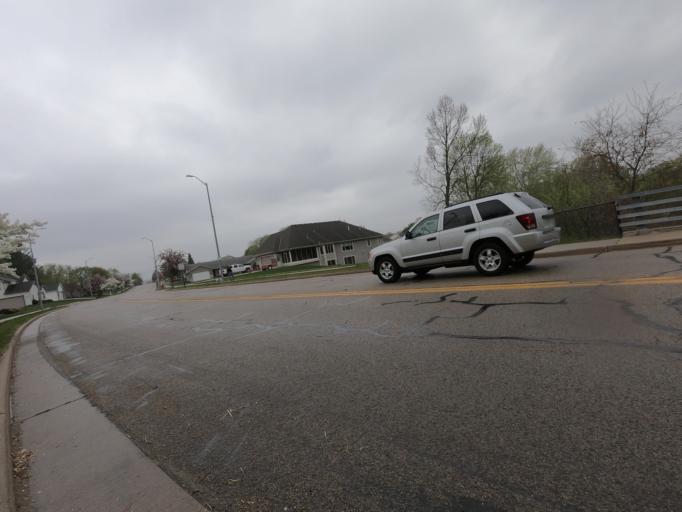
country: US
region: Wisconsin
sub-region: Jefferson County
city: Jefferson
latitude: 43.0123
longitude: -88.8138
